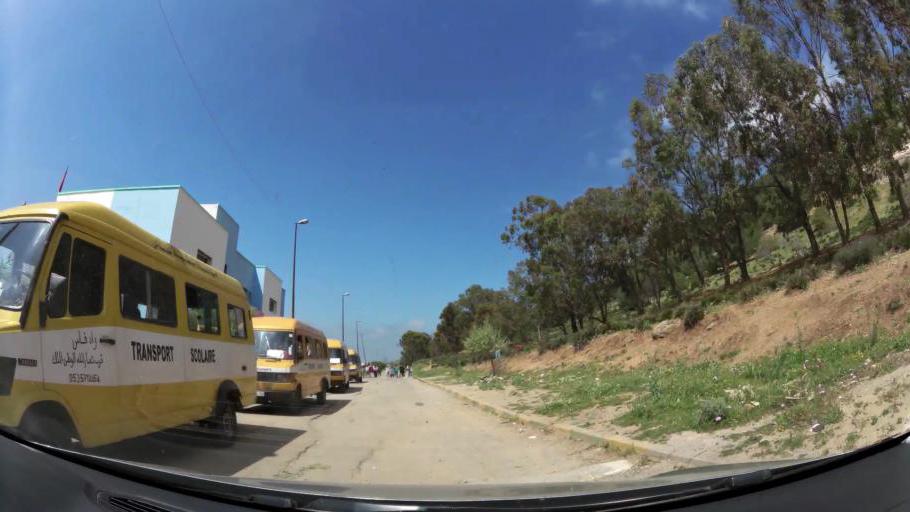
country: MA
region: Fes-Boulemane
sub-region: Fes
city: Fes
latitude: 34.0632
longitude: -5.0339
